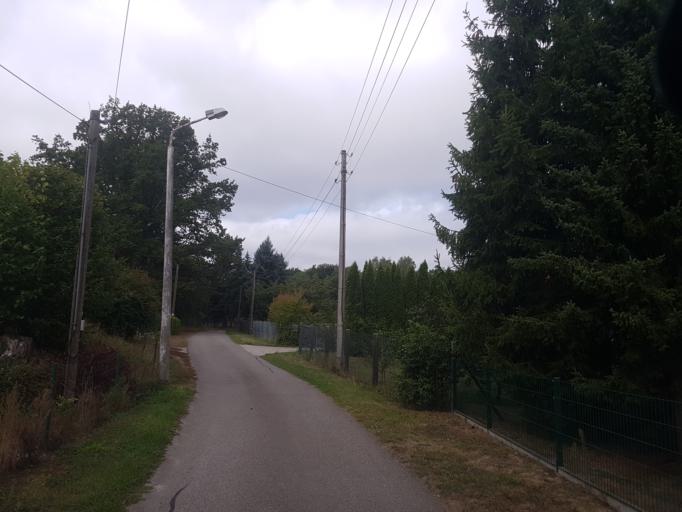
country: DE
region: Brandenburg
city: Calau
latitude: 51.7241
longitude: 13.9453
